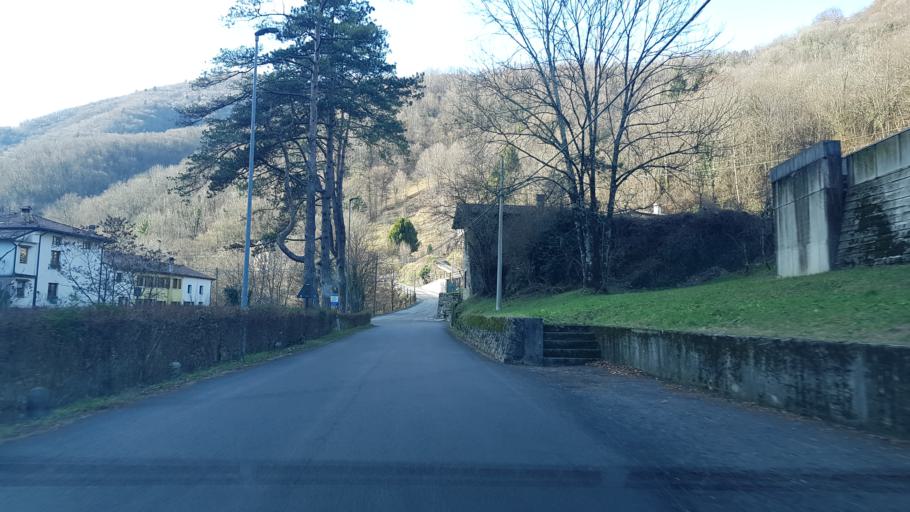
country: IT
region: Friuli Venezia Giulia
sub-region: Provincia di Udine
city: Clodig
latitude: 46.1557
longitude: 13.5864
